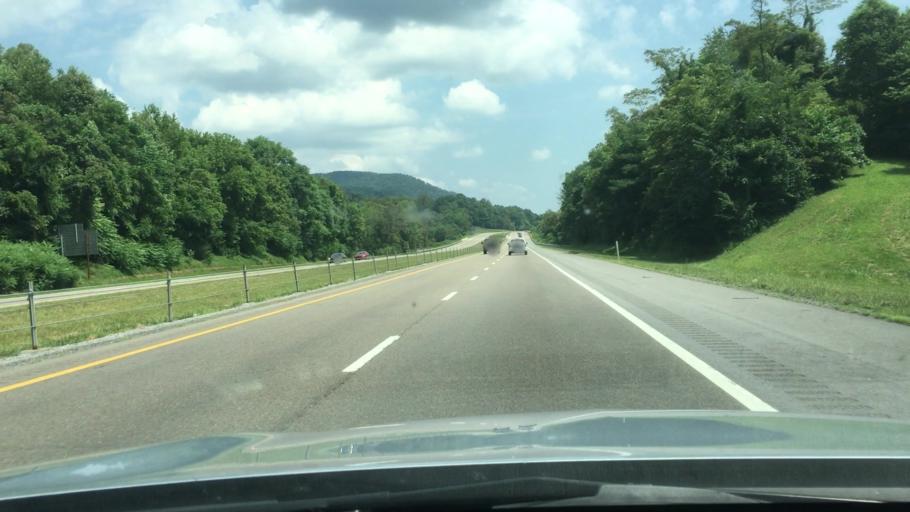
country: US
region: Tennessee
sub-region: Unicoi County
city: Unicoi
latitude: 36.2229
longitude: -82.3420
